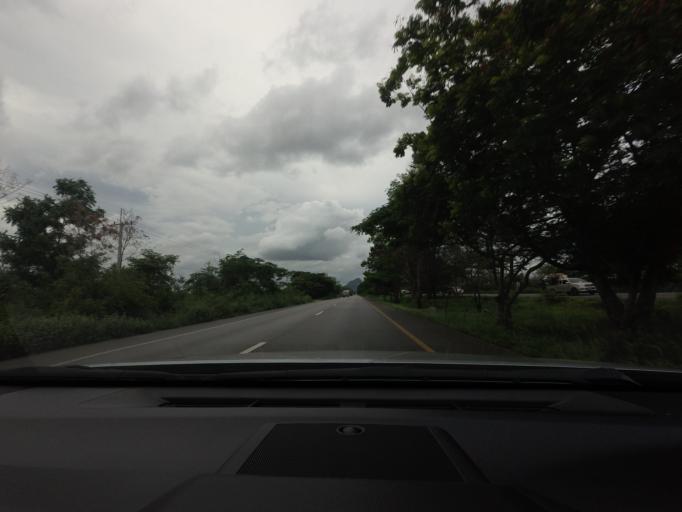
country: TH
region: Phetchaburi
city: Cha-am
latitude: 12.7657
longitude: 99.9345
